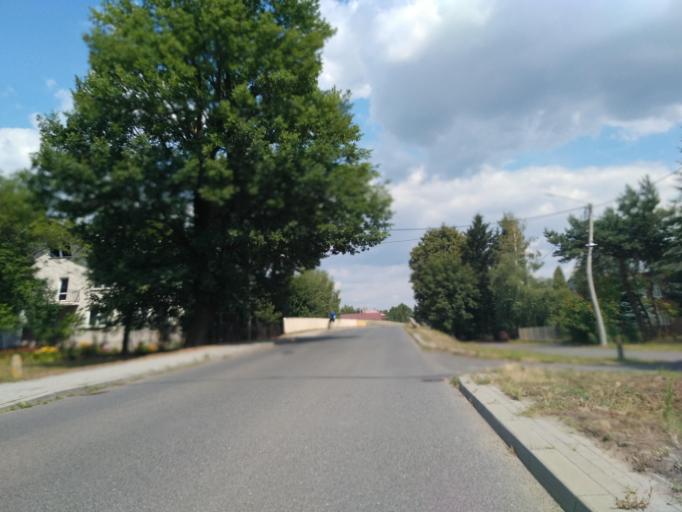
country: PL
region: Subcarpathian Voivodeship
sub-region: Powiat debicki
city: Pilzno
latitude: 49.9853
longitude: 21.2885
